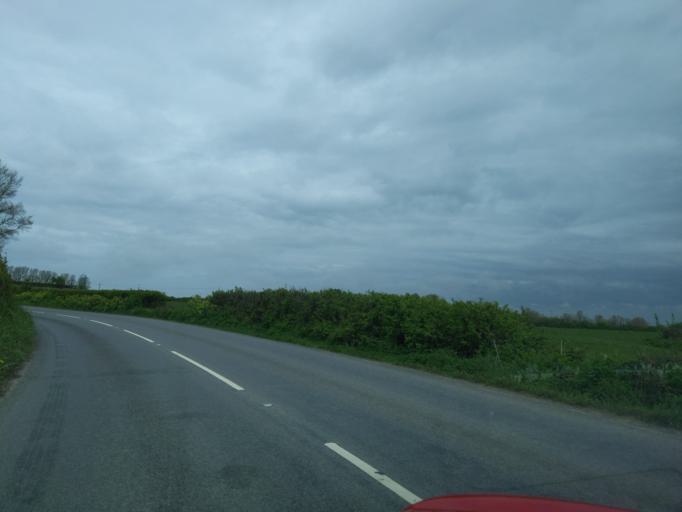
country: GB
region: England
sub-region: Cornwall
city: Wadebridge
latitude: 50.5562
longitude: -4.8635
